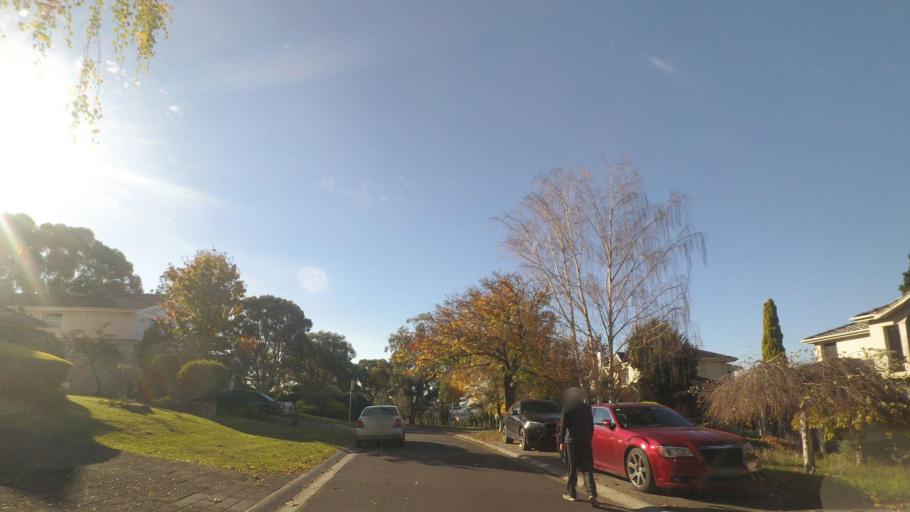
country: AU
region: Victoria
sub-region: Manningham
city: Doncaster East
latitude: -37.7708
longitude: 145.1581
